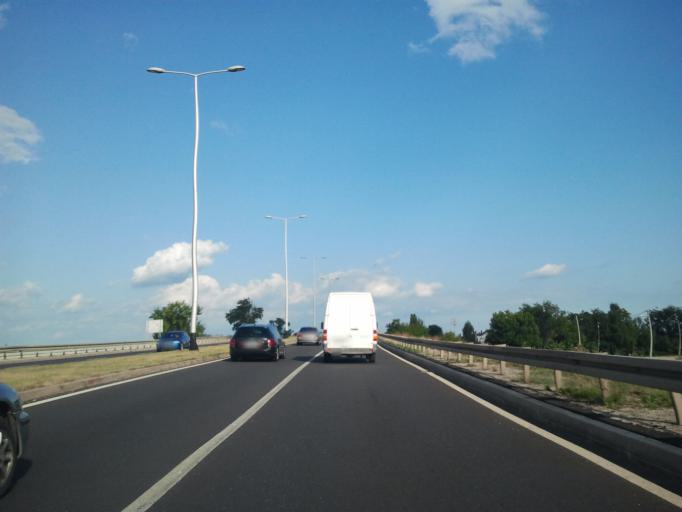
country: HR
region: Grad Zagreb
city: Odra
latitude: 45.7288
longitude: 16.0297
